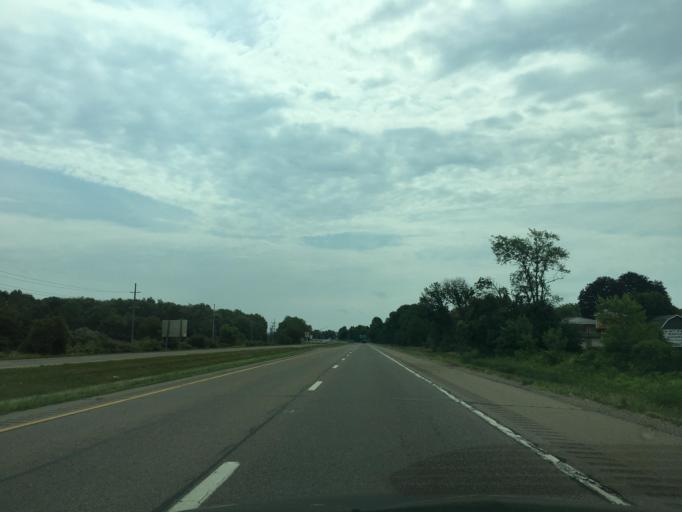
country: US
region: Ohio
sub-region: Tuscarawas County
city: New Philadelphia
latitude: 40.4837
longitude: -81.4607
